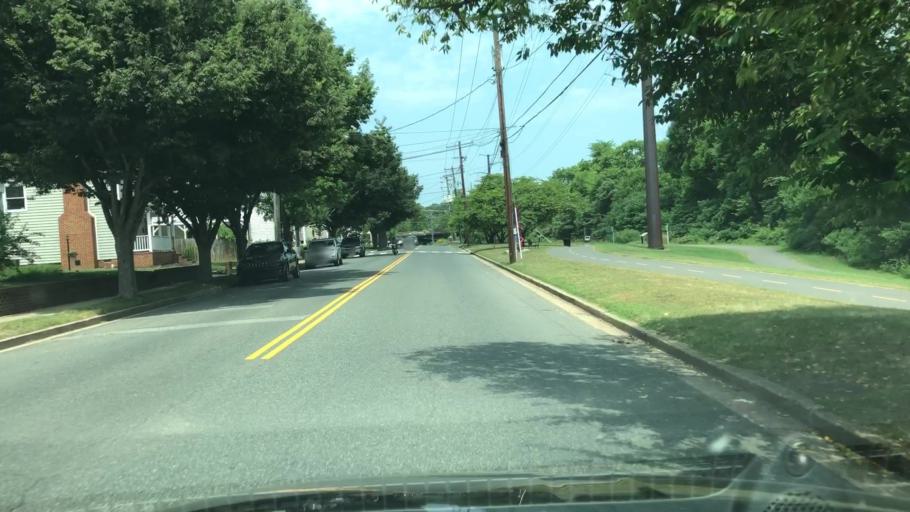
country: US
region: Virginia
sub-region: Stafford County
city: Falmouth
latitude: 38.3171
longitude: -77.4695
